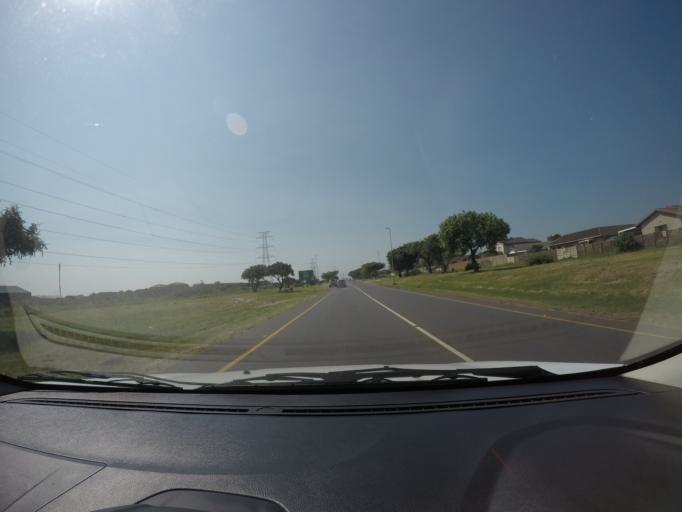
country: ZA
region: KwaZulu-Natal
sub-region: uThungulu District Municipality
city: Richards Bay
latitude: -28.7340
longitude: 32.0401
